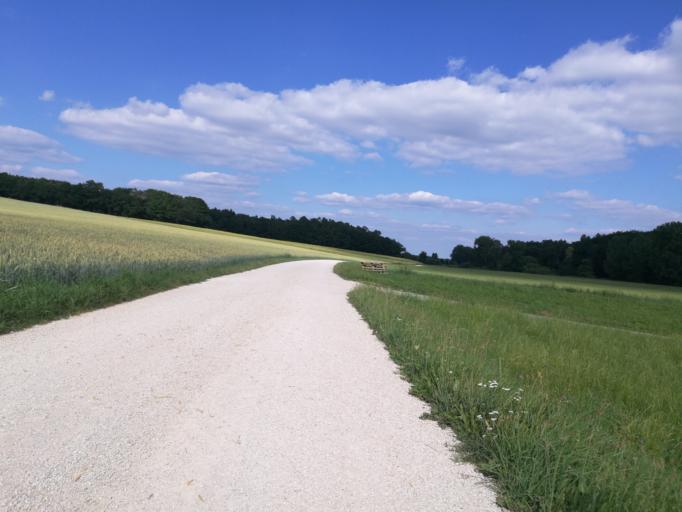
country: DE
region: Bavaria
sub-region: Regierungsbezirk Mittelfranken
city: Veitsbronn
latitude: 49.5078
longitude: 10.9092
